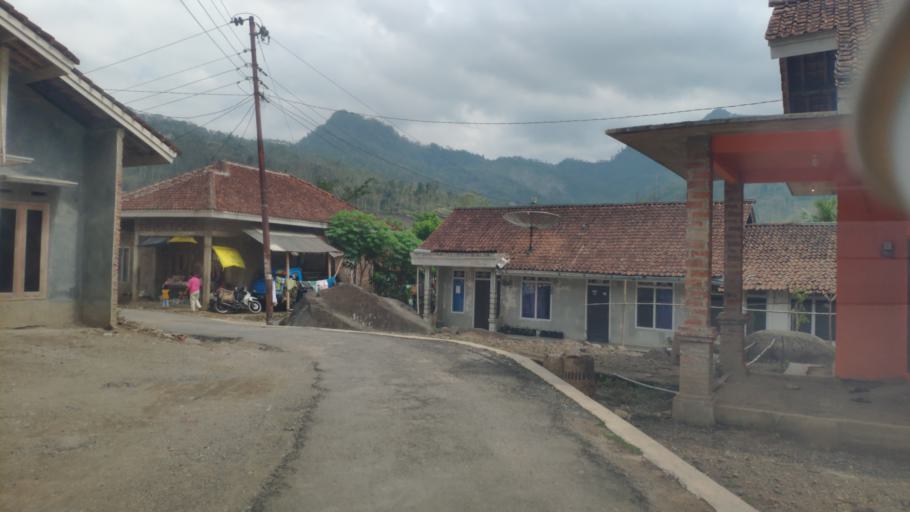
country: ID
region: Central Java
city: Wonosobo
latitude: -7.3223
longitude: 109.7460
